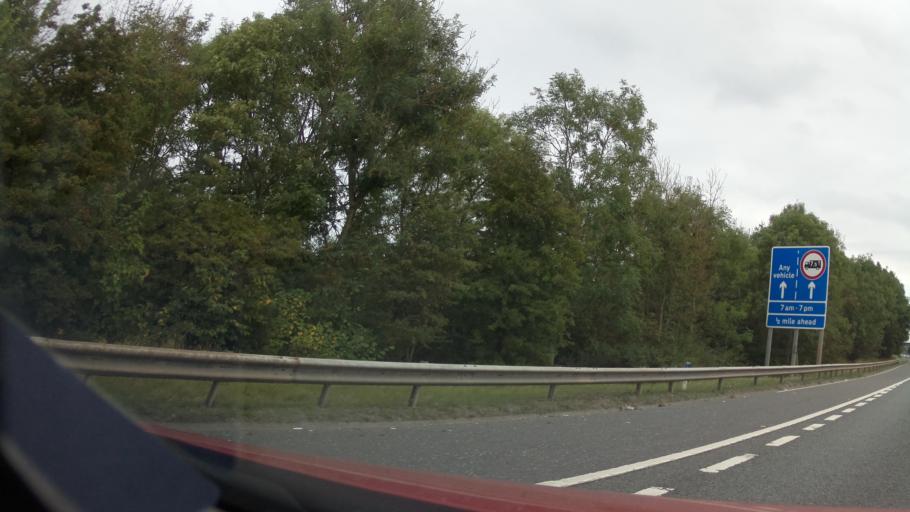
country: GB
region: England
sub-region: County Durham
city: Chester-le-Street
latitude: 54.8614
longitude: -1.5594
